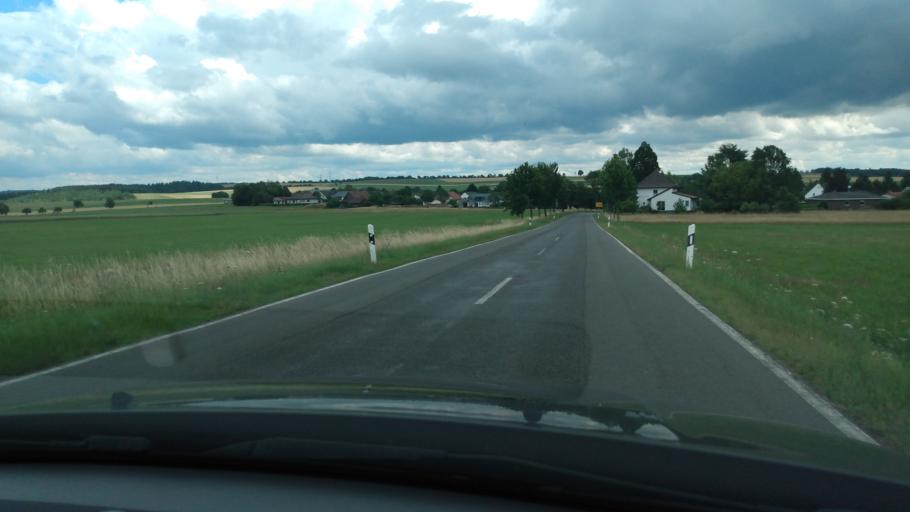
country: DE
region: Rheinland-Pfalz
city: Grosslittgen
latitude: 50.0316
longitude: 6.7938
